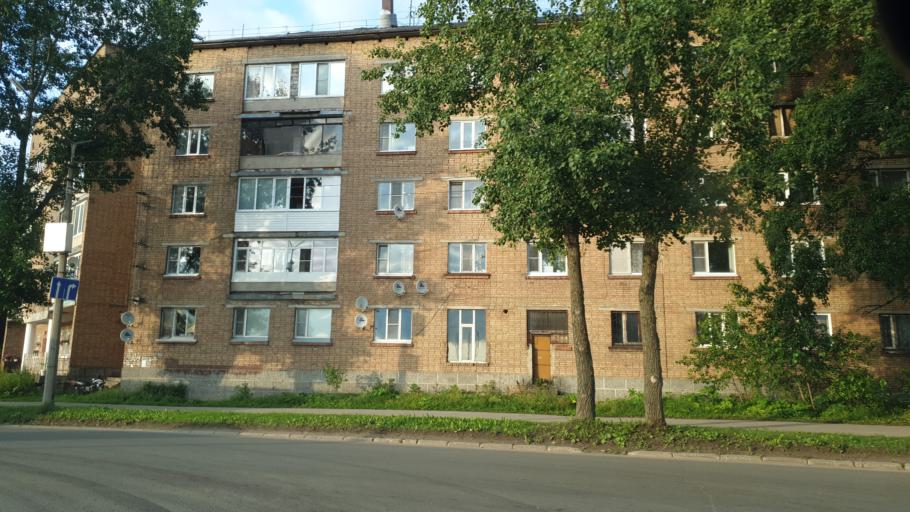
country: RU
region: Komi Republic
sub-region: Syktyvdinskiy Rayon
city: Syktyvkar
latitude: 61.6636
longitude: 50.7892
